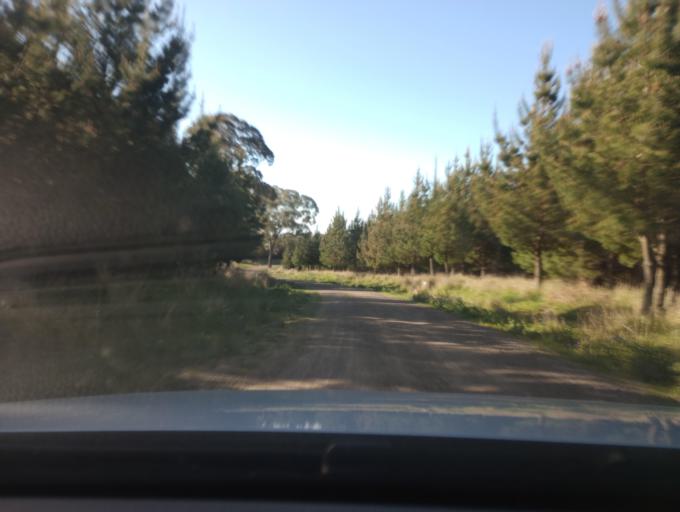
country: AU
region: New South Wales
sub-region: Blayney
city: Millthorpe
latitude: -33.4134
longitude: 149.3132
